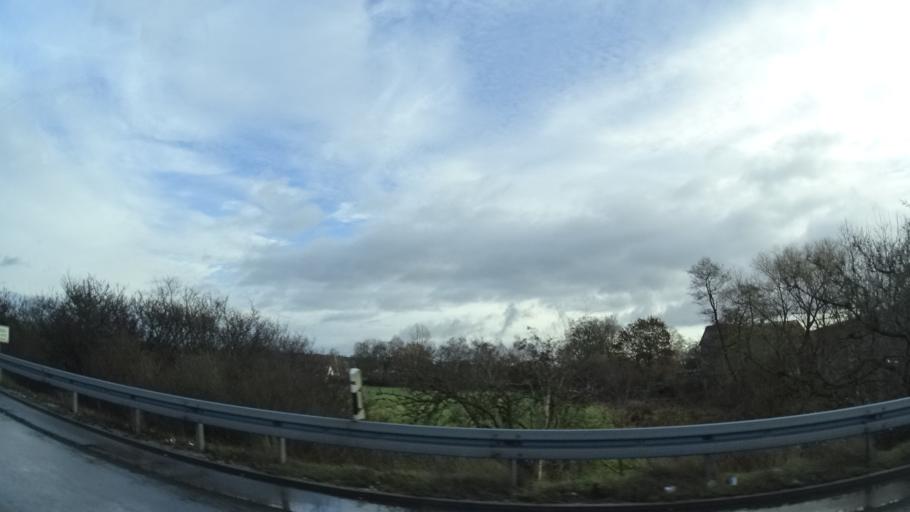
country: DE
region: Hesse
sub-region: Regierungsbezirk Darmstadt
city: Ober-Morlen
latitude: 50.3802
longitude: 8.7054
